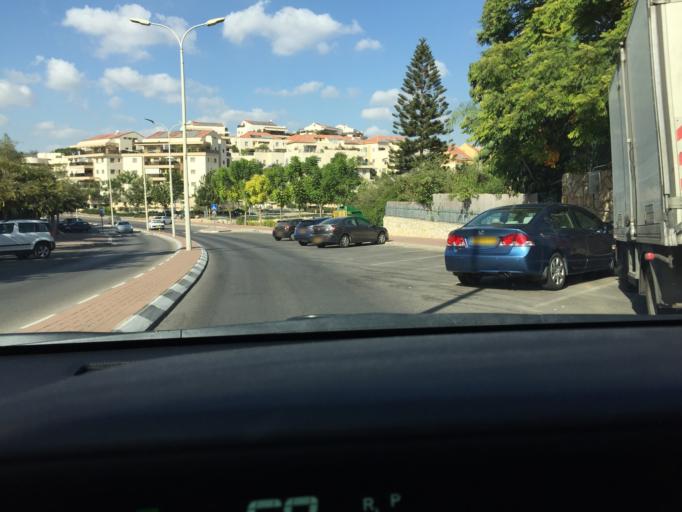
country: PS
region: West Bank
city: Budrus
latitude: 32.0017
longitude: 34.9483
